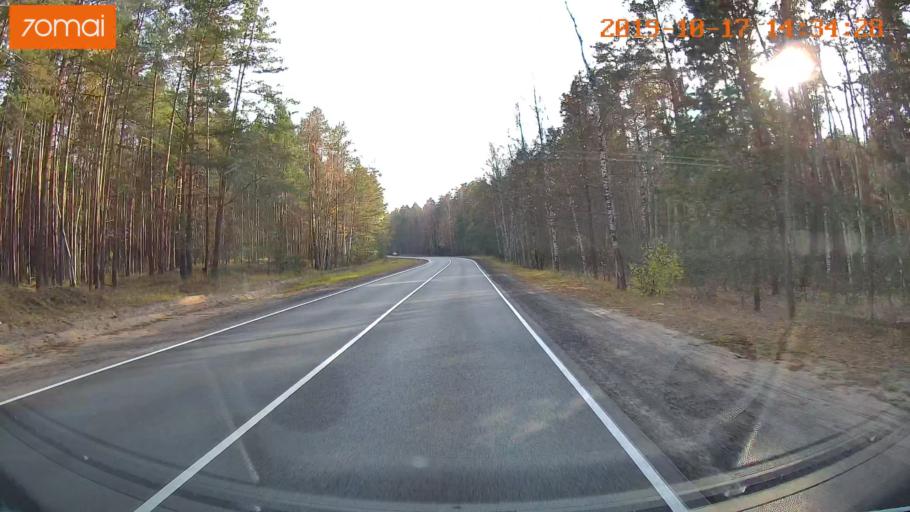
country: RU
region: Rjazan
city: Solotcha
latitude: 54.9121
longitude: 39.9978
